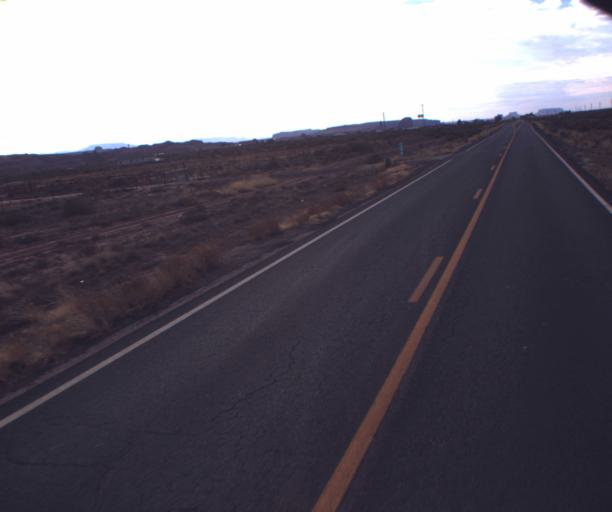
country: US
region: Arizona
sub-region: Apache County
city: Many Farms
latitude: 36.7303
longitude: -109.6318
